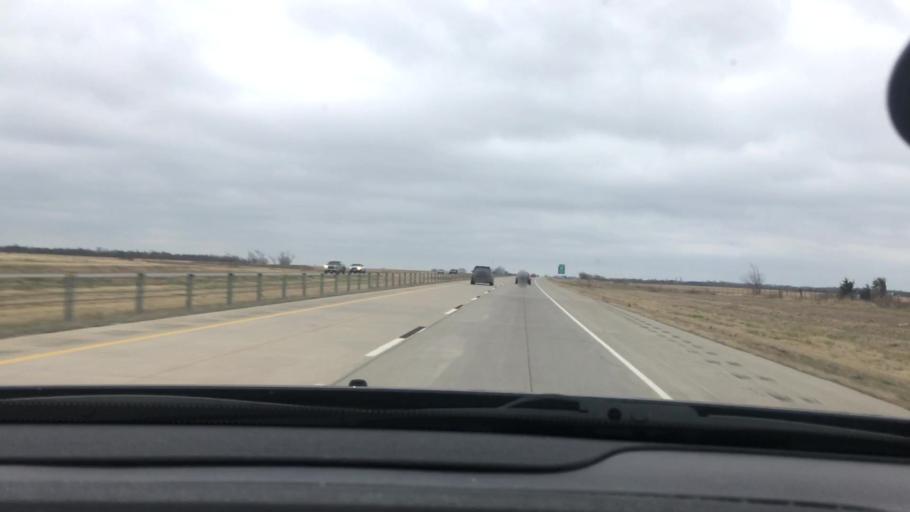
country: US
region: Oklahoma
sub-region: Bryan County
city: Durant
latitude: 34.1154
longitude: -96.2960
